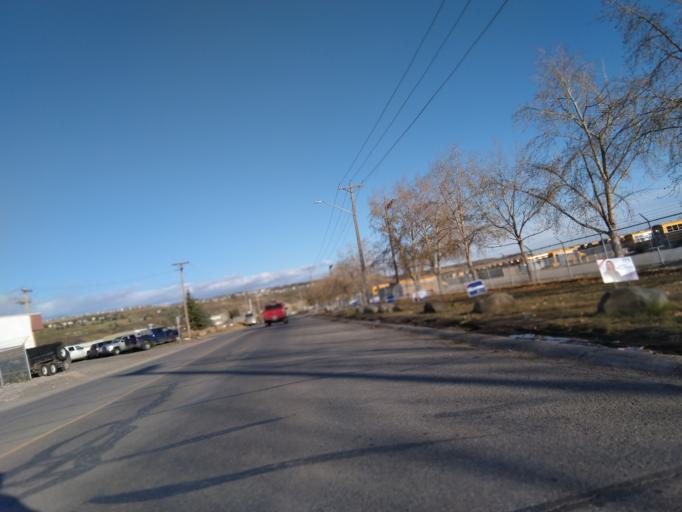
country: CA
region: Alberta
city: Cochrane
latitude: 51.1833
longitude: -114.4636
